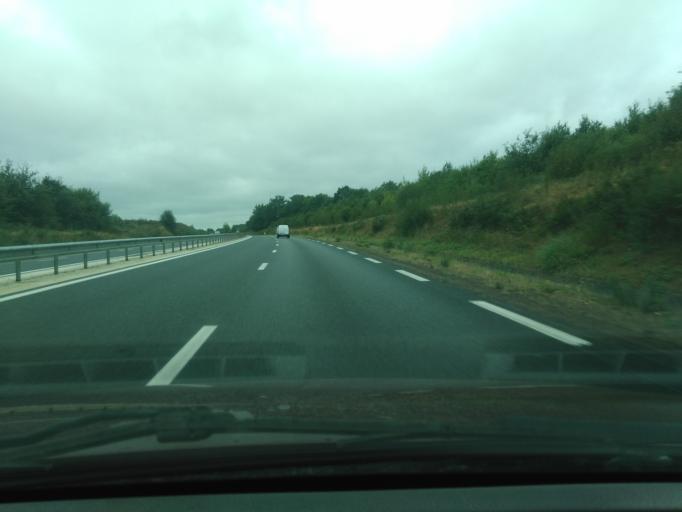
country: FR
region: Pays de la Loire
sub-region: Departement de la Vendee
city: La Roche-sur-Yon
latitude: 46.6798
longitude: -1.3769
